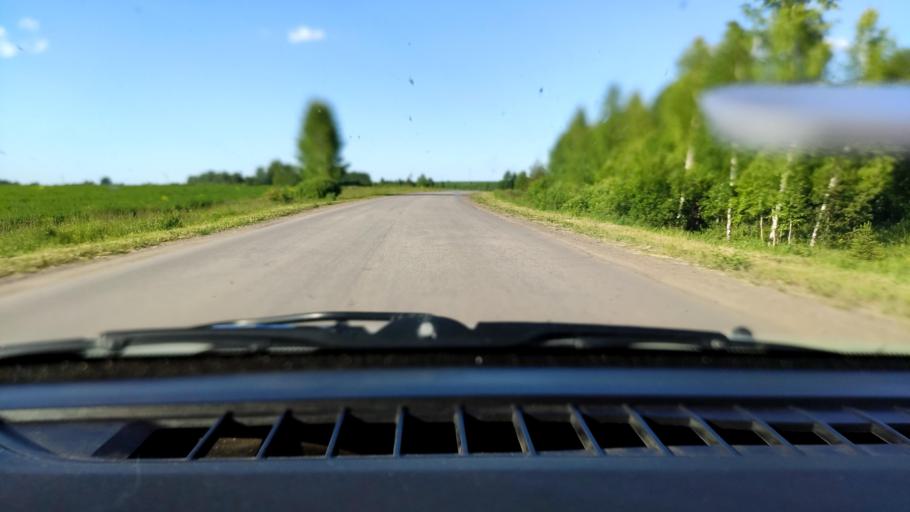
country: RU
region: Perm
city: Orda
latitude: 57.1870
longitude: 56.8489
